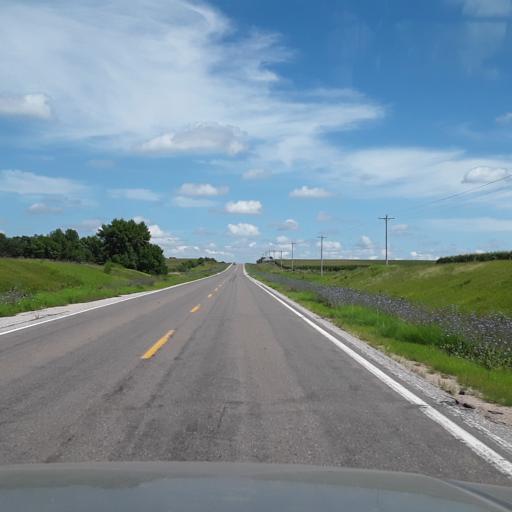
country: US
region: Nebraska
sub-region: York County
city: York
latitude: 40.9861
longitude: -97.4063
